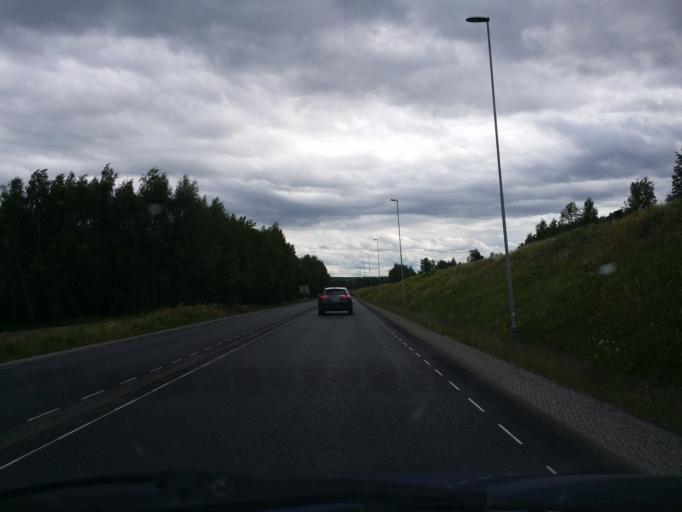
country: NO
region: Hedmark
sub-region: Hamar
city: Hamar
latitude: 60.8212
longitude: 11.0922
